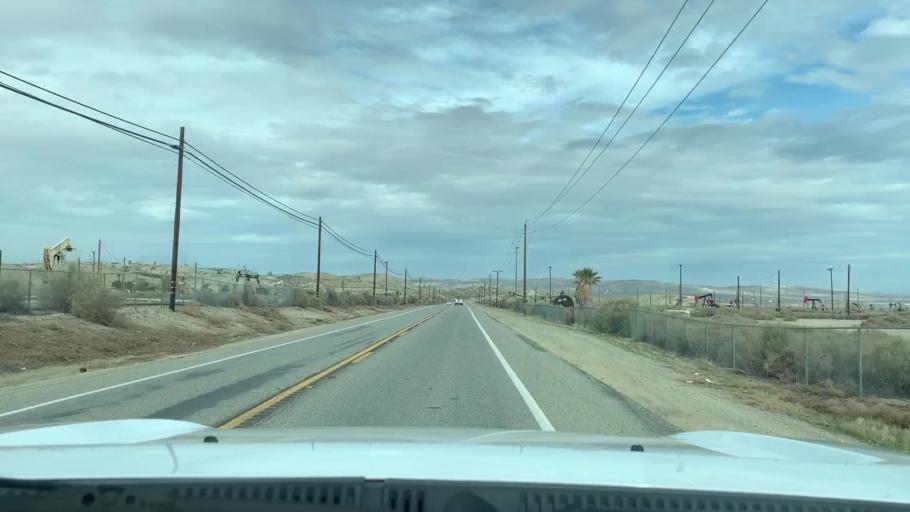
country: US
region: California
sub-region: Kern County
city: Maricopa
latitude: 35.0673
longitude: -119.4020
